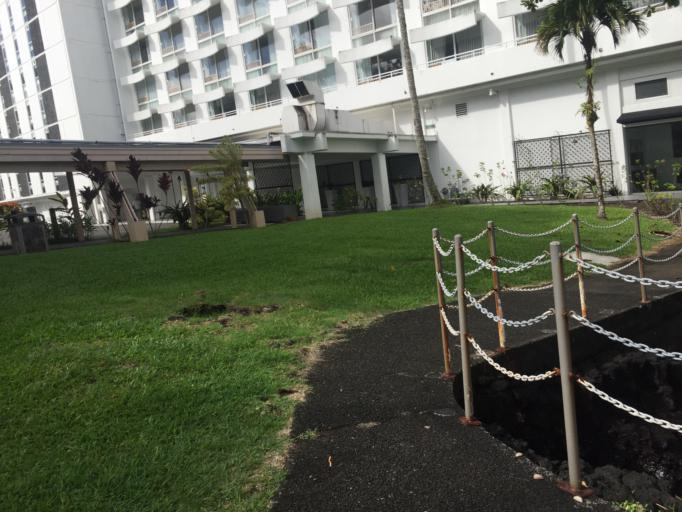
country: US
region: Hawaii
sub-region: Hawaii County
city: Hilo
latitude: 19.7300
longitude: -155.0646
